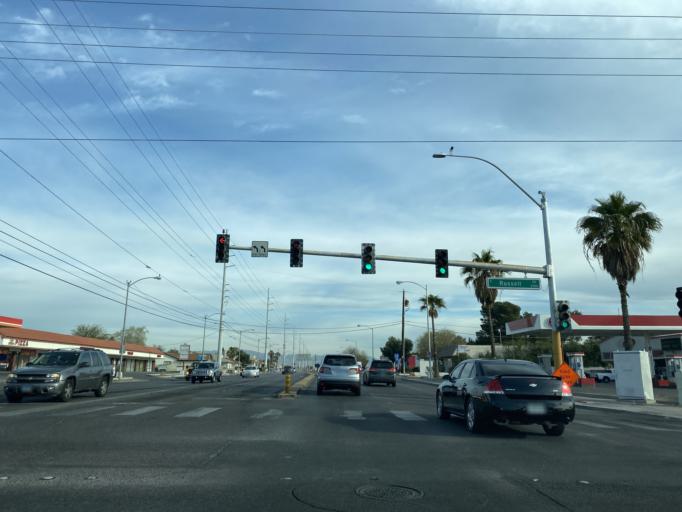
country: US
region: Nevada
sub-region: Clark County
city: Paradise
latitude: 36.0863
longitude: -115.1187
